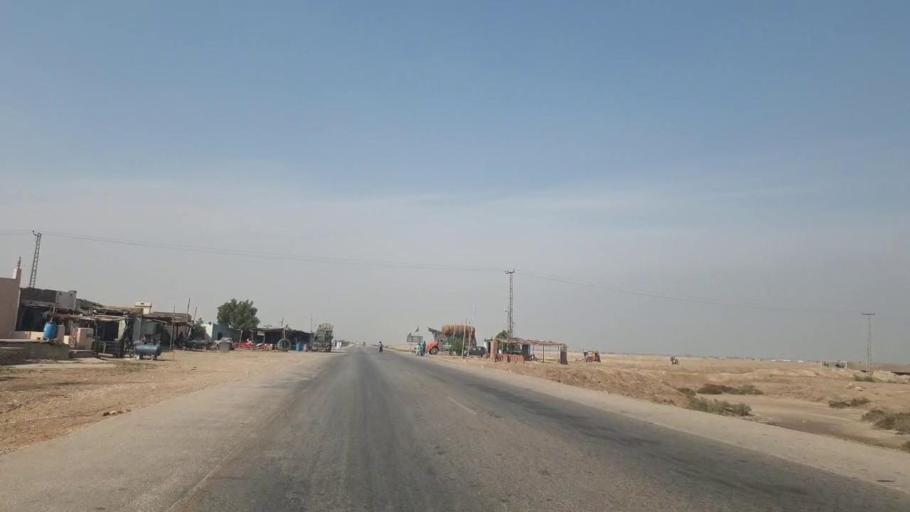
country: PK
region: Sindh
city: Sann
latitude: 25.9019
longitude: 68.2317
